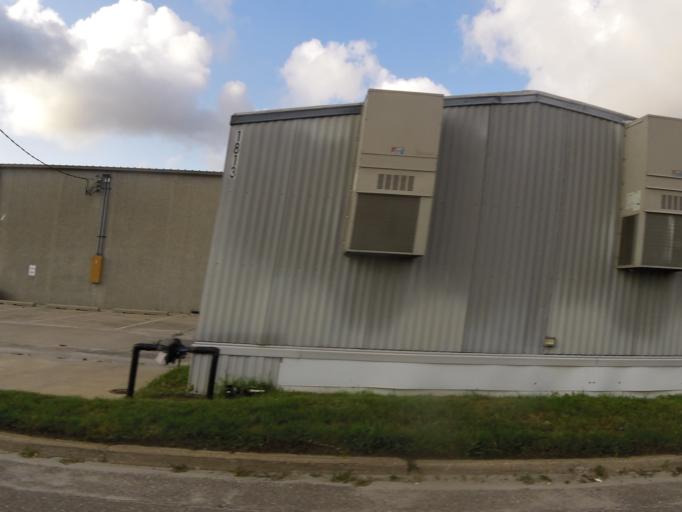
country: US
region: Florida
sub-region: Duval County
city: Jacksonville
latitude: 30.3291
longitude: -81.6797
